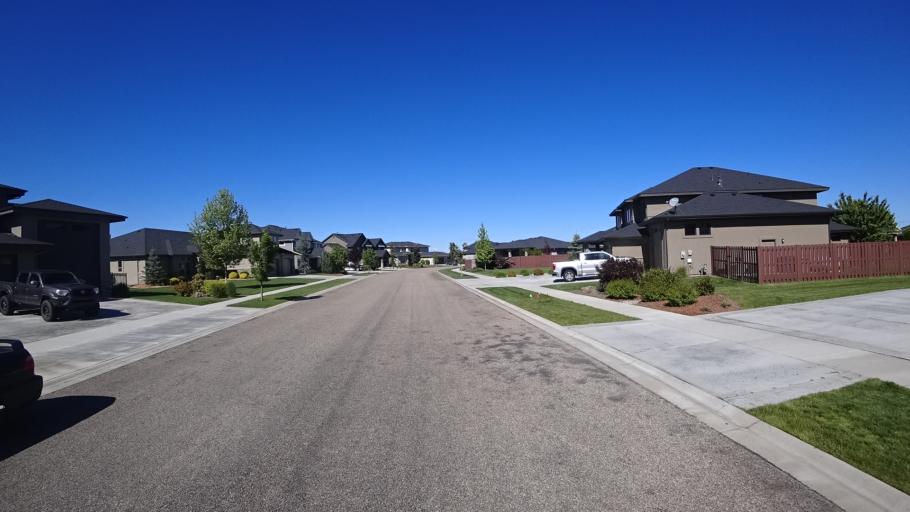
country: US
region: Idaho
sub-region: Ada County
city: Meridian
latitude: 43.6670
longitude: -116.4038
